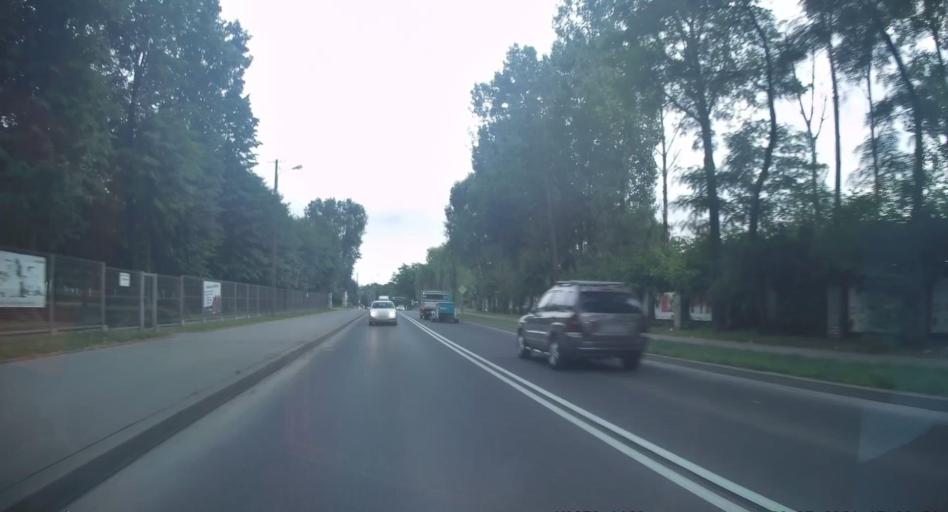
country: PL
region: Lodz Voivodeship
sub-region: Powiat radomszczanski
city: Radomsko
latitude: 51.0723
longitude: 19.4465
